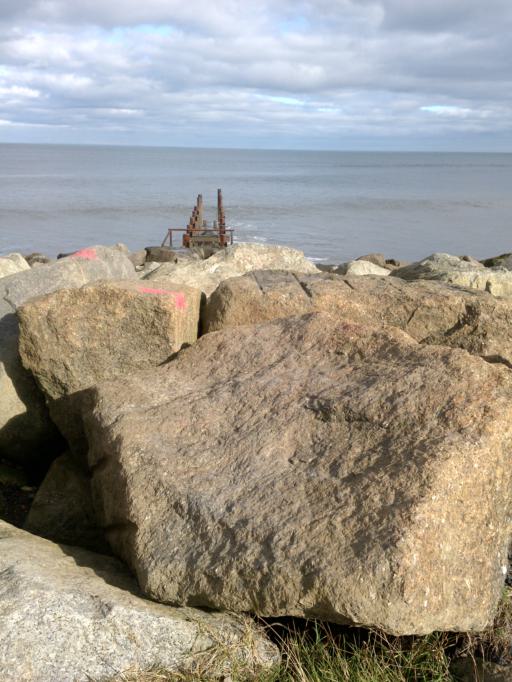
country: GB
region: England
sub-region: Northumberland
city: Newbiggin-by-the-Sea
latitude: 55.2049
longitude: -1.5171
